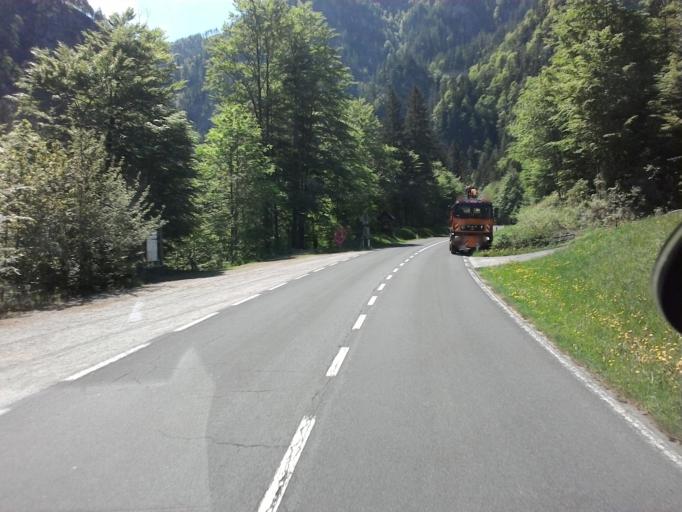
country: AT
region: Styria
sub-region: Politischer Bezirk Liezen
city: Palfau
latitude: 47.6978
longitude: 14.8737
